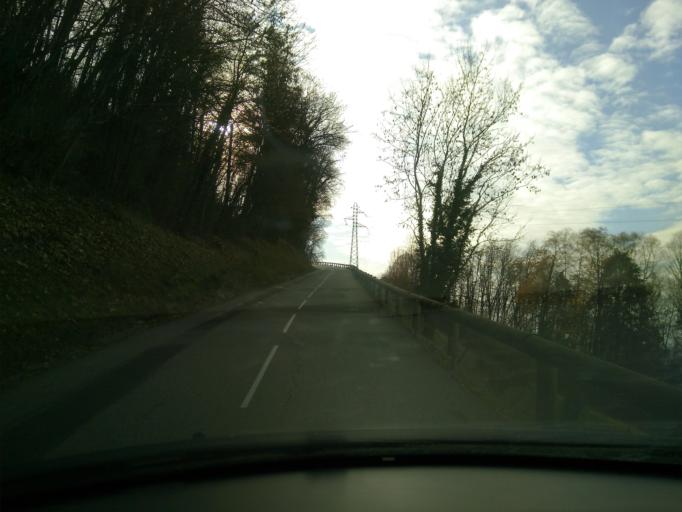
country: FR
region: Rhone-Alpes
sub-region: Departement de l'Isere
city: Villard-Bonnot
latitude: 45.2470
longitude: 5.9063
